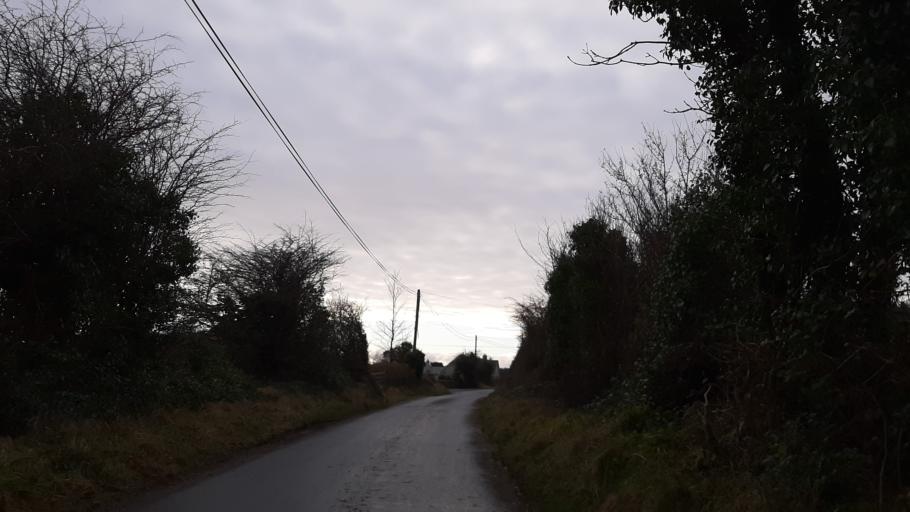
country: IE
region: Connaught
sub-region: County Galway
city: Gaillimh
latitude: 53.3083
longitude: -9.0683
